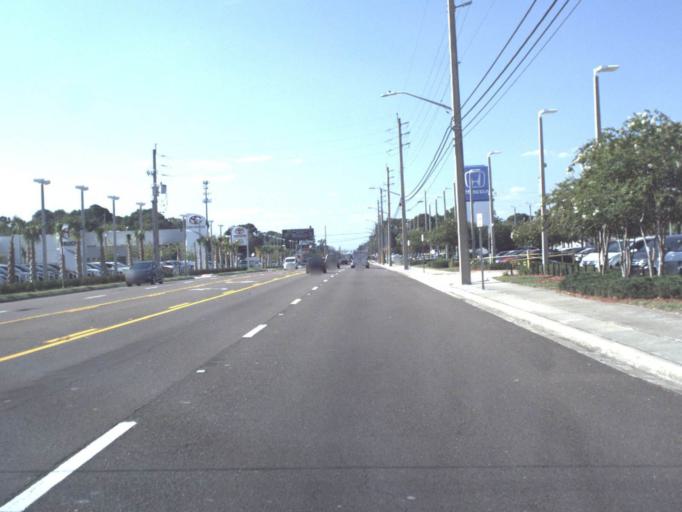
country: US
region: Florida
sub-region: Duval County
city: Jacksonville
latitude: 30.2976
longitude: -81.7304
